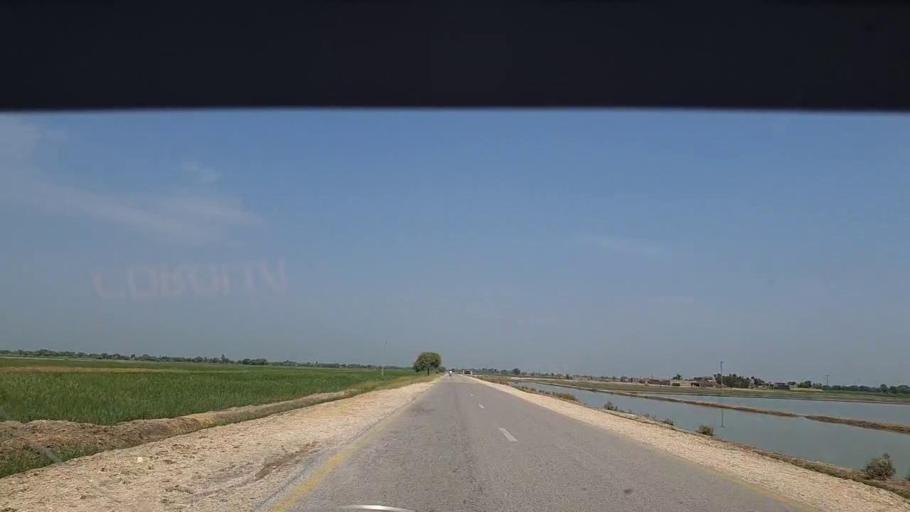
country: PK
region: Sindh
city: Rustam jo Goth
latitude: 28.0933
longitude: 68.8002
